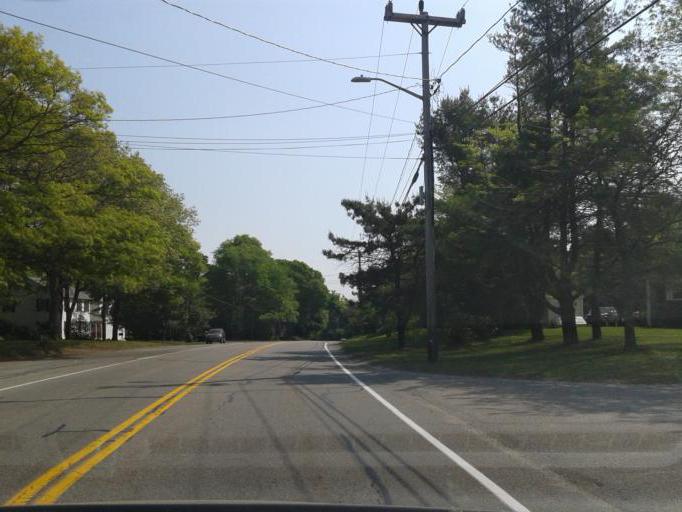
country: US
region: Massachusetts
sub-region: Barnstable County
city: East Falmouth
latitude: 41.5961
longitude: -70.5759
